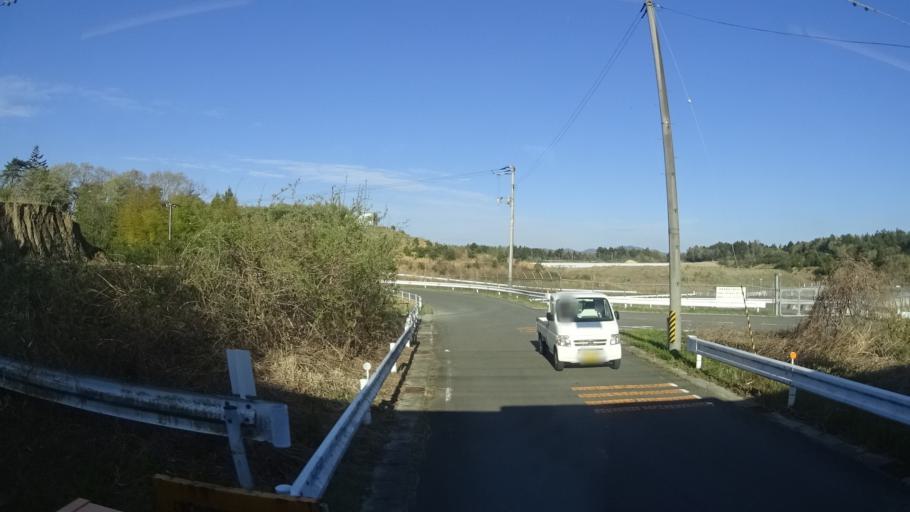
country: JP
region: Fukushima
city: Namie
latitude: 37.6722
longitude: 140.9720
